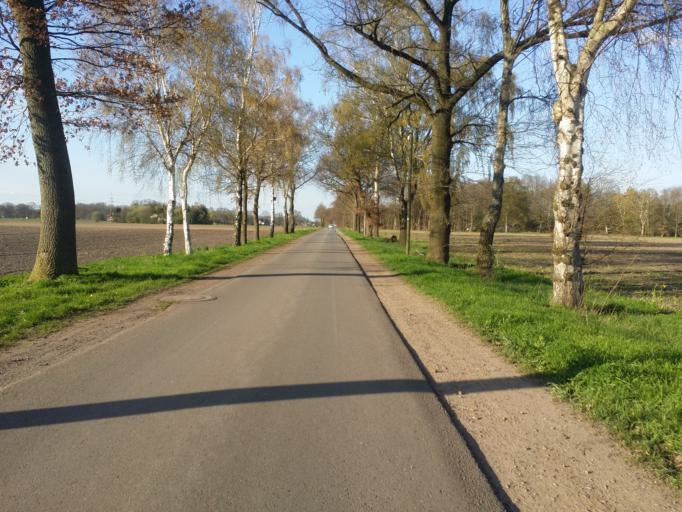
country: DE
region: Lower Saxony
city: Gross Ippener
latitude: 53.0056
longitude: 8.6391
